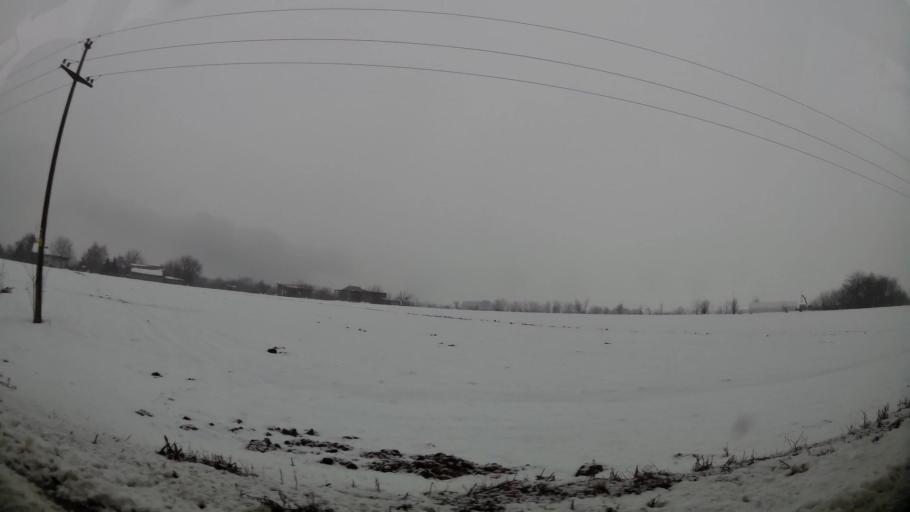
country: RS
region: Central Serbia
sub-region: Belgrade
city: Zemun
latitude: 44.8416
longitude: 20.3513
